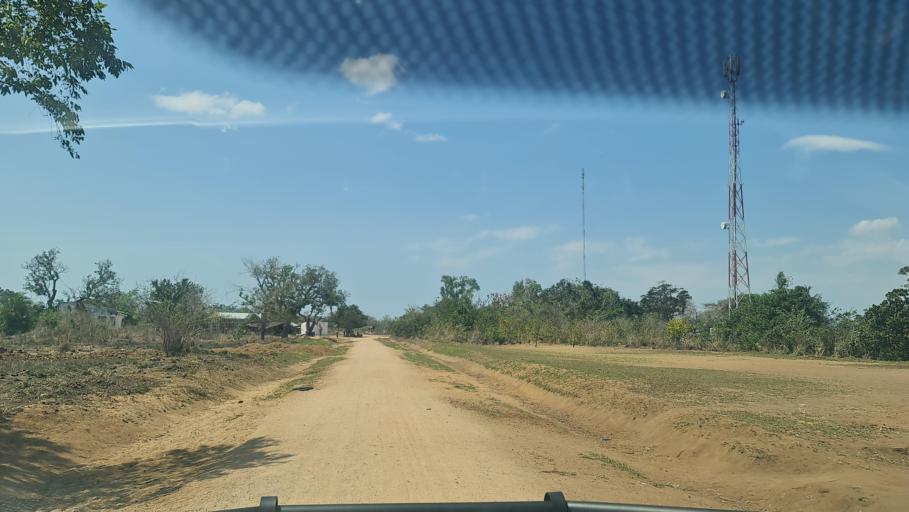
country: MZ
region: Nampula
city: Ilha de Mocambique
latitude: -15.1946
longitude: 40.5243
